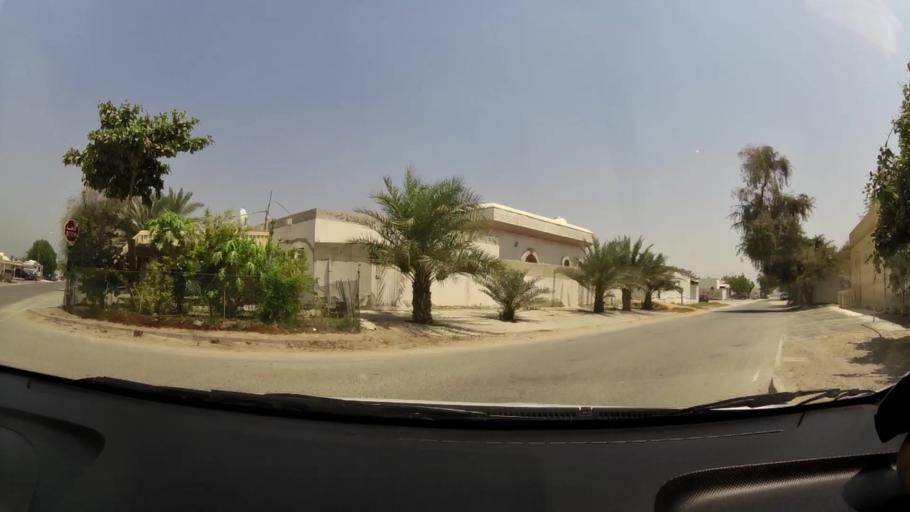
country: AE
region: Umm al Qaywayn
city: Umm al Qaywayn
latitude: 25.5595
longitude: 55.5605
